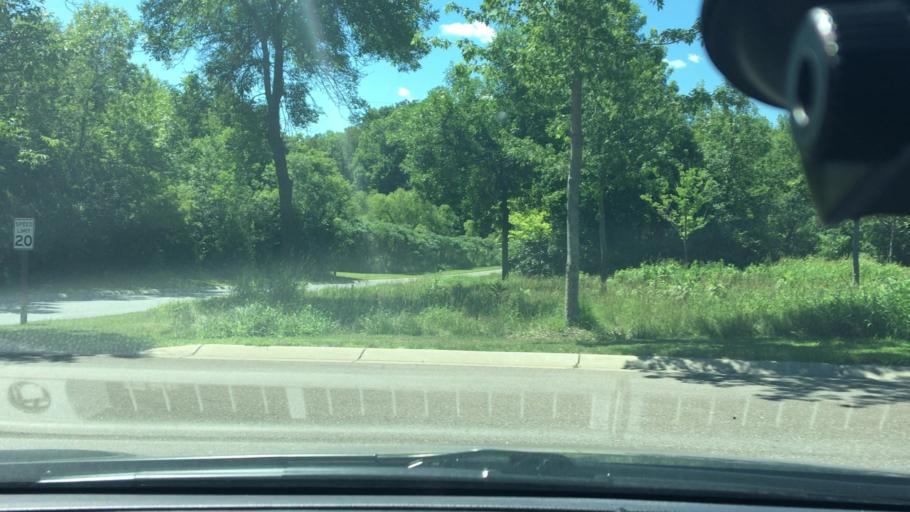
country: US
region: Minnesota
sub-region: Hennepin County
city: Maple Grove
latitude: 45.0808
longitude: -93.4642
